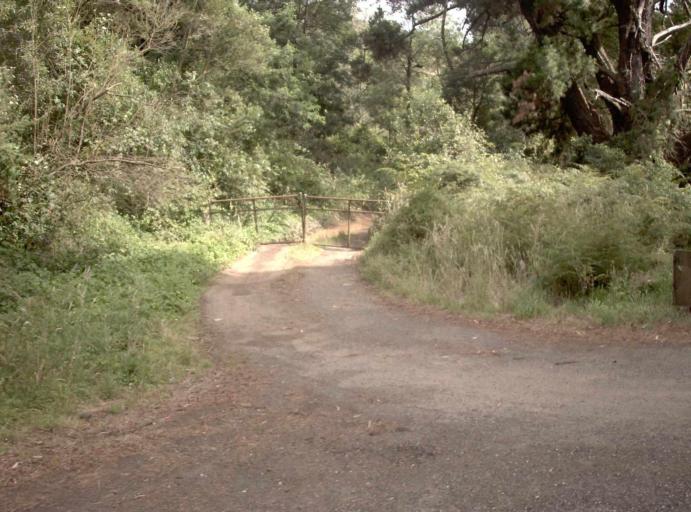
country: AU
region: Victoria
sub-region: Latrobe
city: Moe
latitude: -38.2581
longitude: 146.1845
